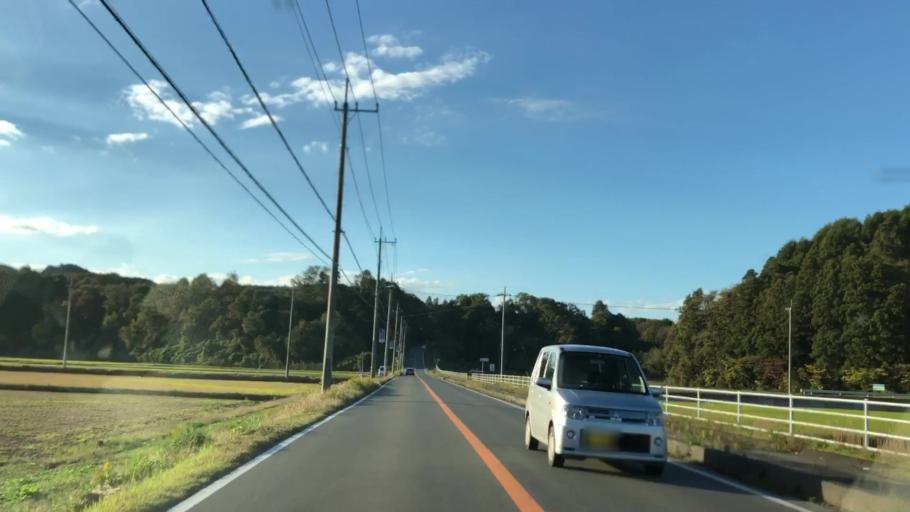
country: JP
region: Ibaraki
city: Kasama
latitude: 36.4455
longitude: 140.3600
